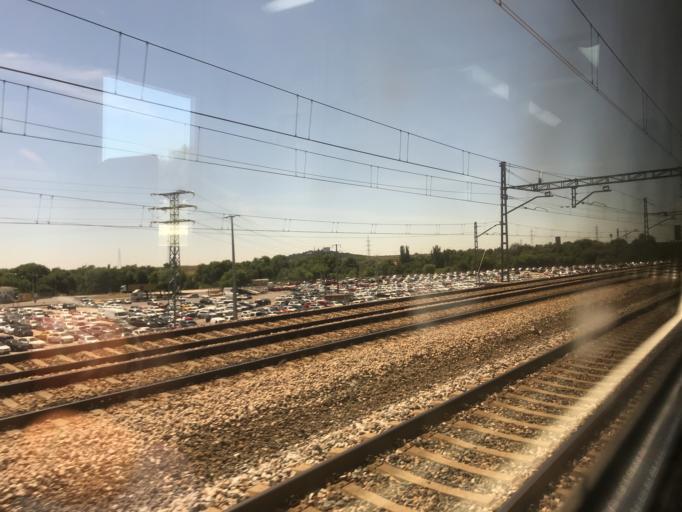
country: ES
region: Madrid
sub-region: Provincia de Madrid
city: Villaverde
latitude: 40.3362
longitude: -3.6853
